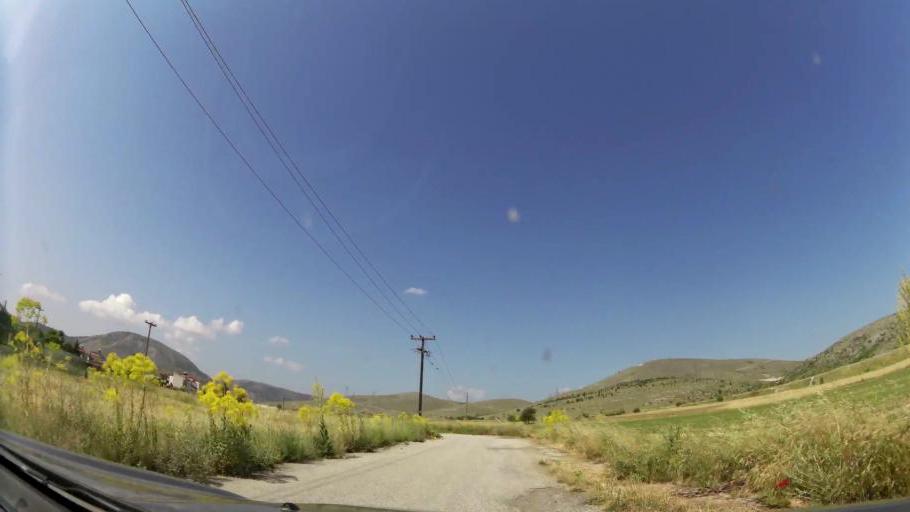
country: GR
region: West Macedonia
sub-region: Nomos Kozanis
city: Koila
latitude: 40.3407
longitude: 21.7878
